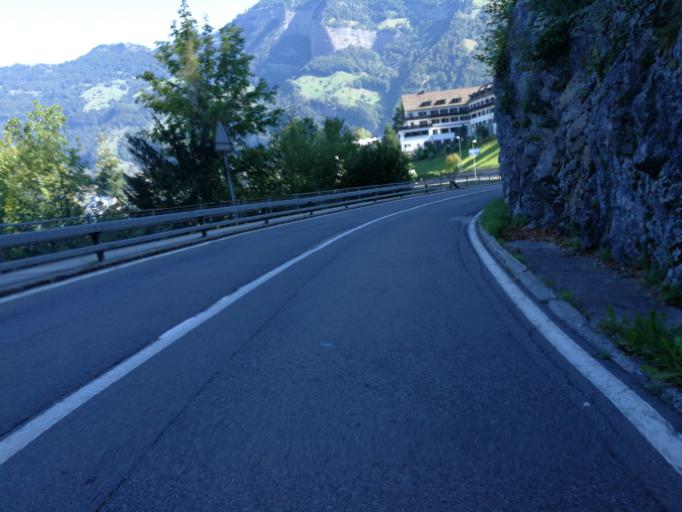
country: CH
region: Lucerne
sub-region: Lucerne-Land District
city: Vitznau
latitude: 46.9973
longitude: 8.4768
